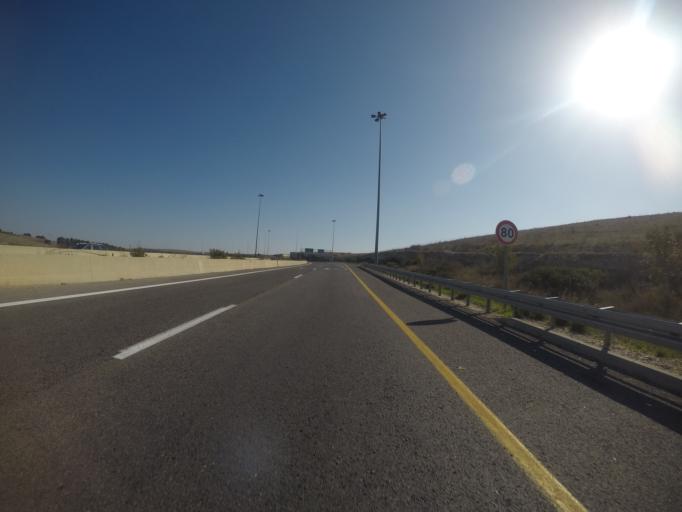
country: IL
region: Haifa
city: Daliyat el Karmil
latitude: 32.6101
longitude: 35.0399
